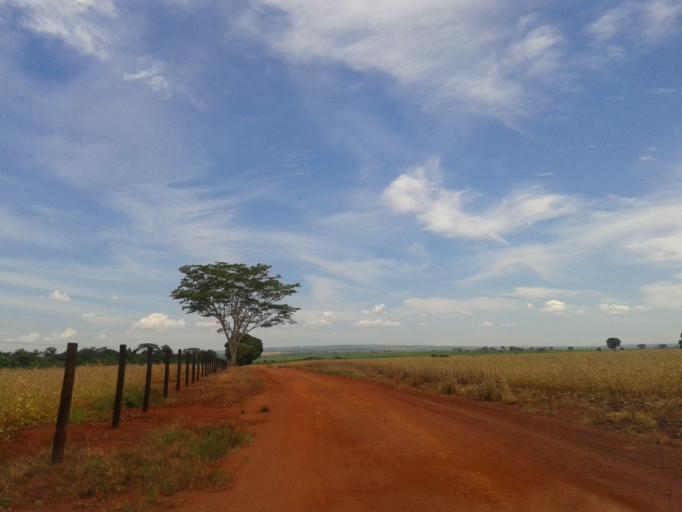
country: BR
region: Minas Gerais
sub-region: Capinopolis
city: Capinopolis
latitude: -18.6658
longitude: -49.7279
